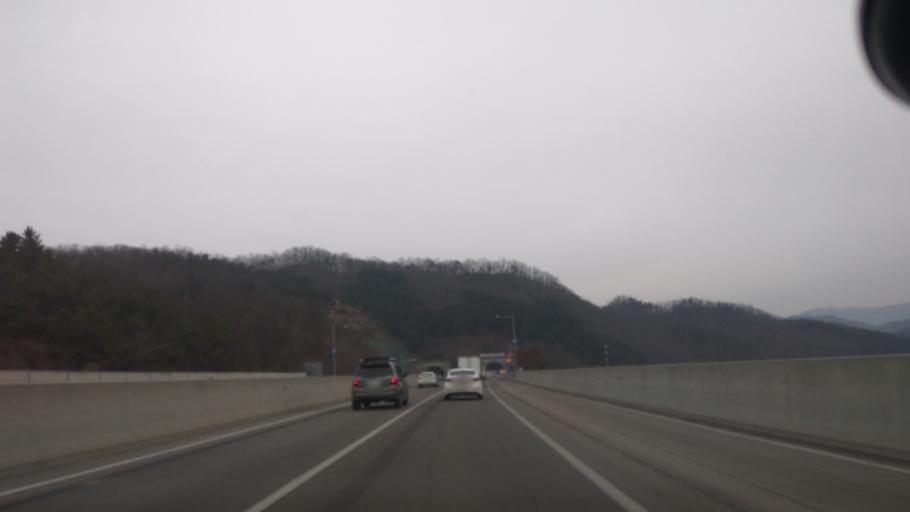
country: KR
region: Gangwon-do
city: Sindong
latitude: 37.7424
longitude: 127.6782
